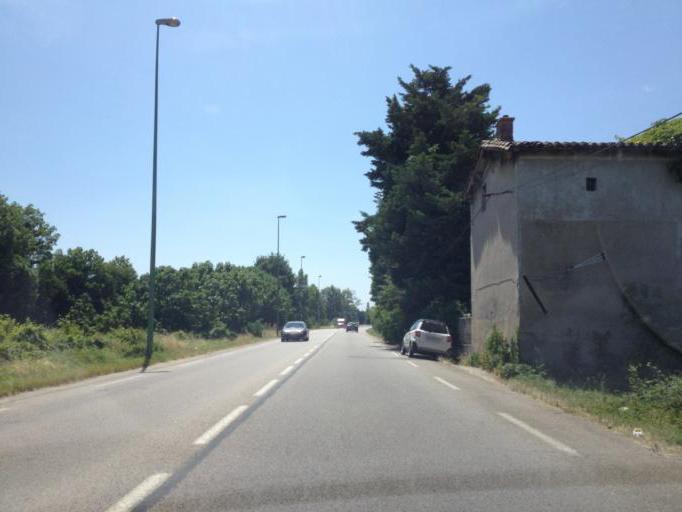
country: FR
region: Rhone-Alpes
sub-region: Departement de l'Ardeche
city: Guilherand-Granges
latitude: 44.9230
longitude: 4.8802
